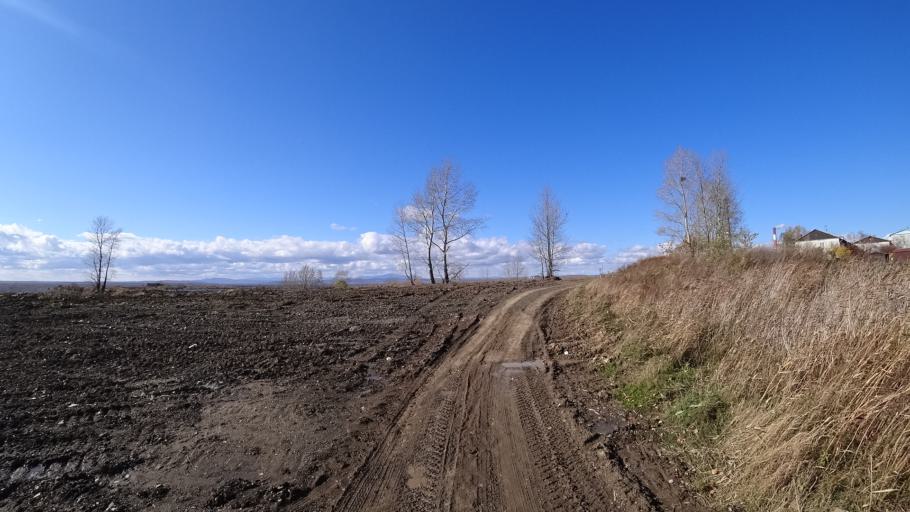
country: RU
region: Khabarovsk Krai
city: Amursk
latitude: 50.2146
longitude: 136.8895
